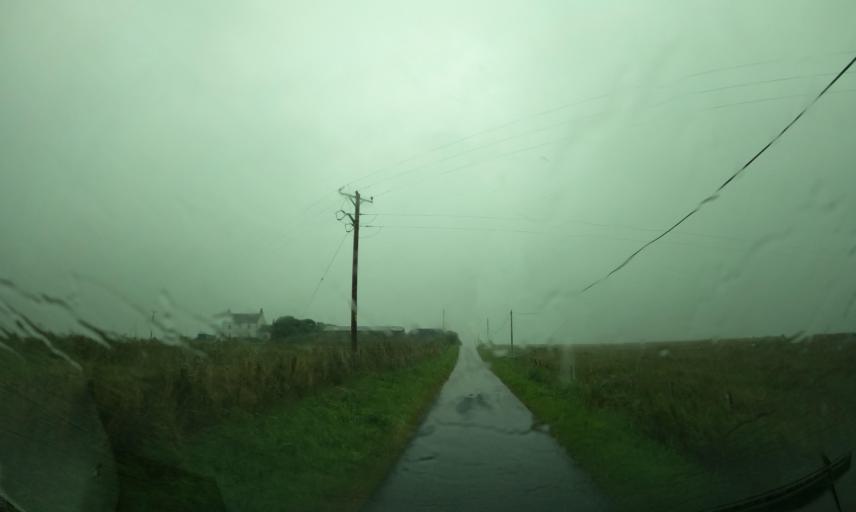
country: GB
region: Scotland
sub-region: Eilean Siar
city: Barra
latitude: 56.4649
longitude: -6.9253
